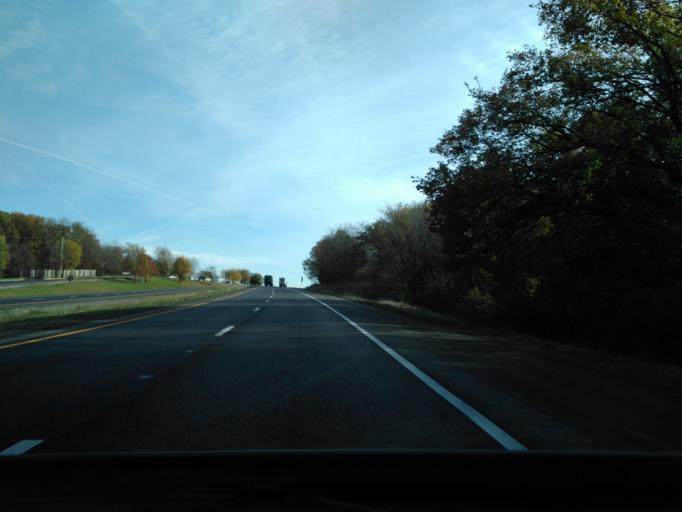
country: US
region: Illinois
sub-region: Madison County
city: Highland
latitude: 38.7864
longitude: -89.6924
